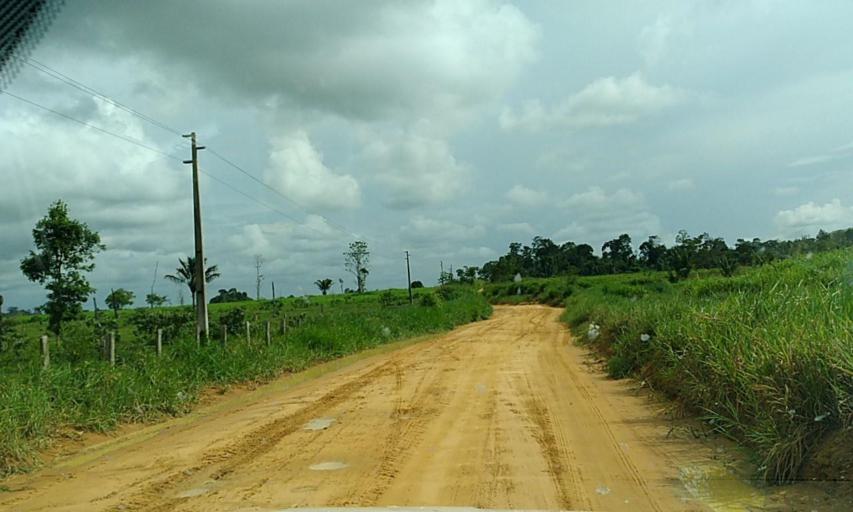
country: BR
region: Para
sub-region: Altamira
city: Altamira
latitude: -3.2328
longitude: -52.6954
